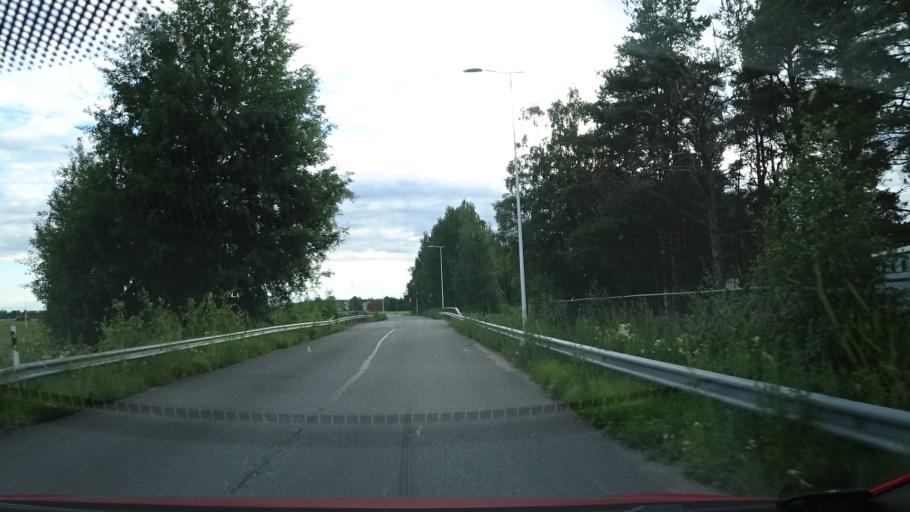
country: FI
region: Northern Ostrobothnia
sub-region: Oulu
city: Liminka
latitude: 64.8099
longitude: 25.4668
